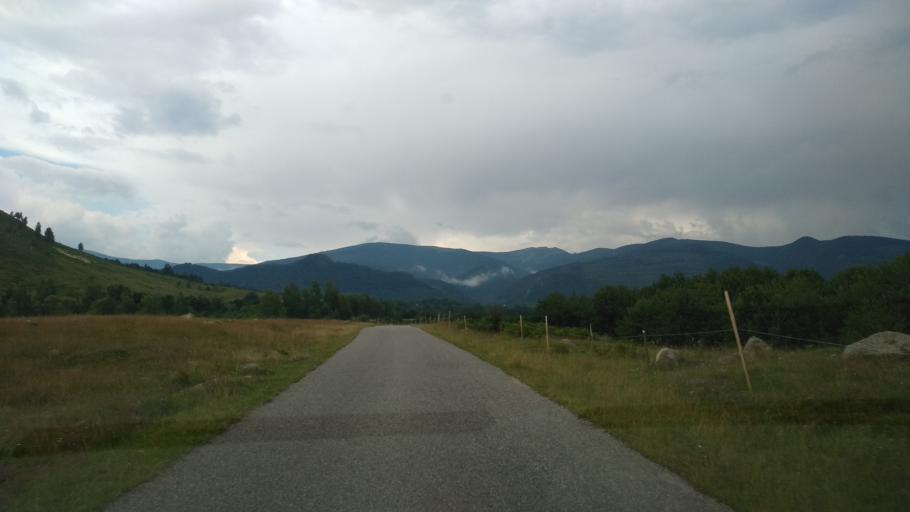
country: RO
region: Hunedoara
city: Salasu de Sus
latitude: 45.4856
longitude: 22.9647
